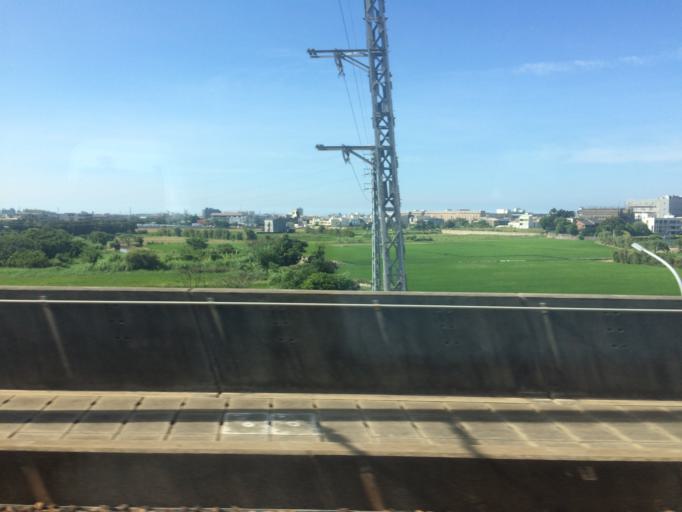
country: TW
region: Taiwan
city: Taoyuan City
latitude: 24.9584
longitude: 121.1563
